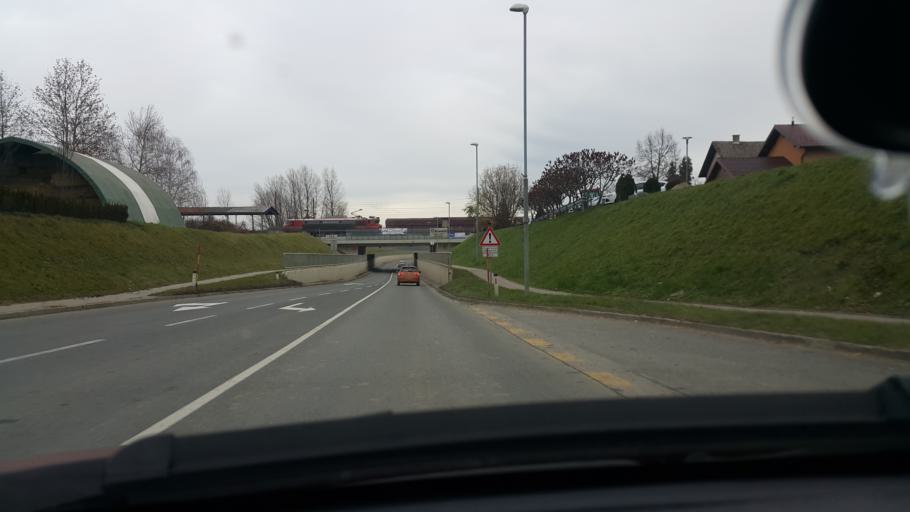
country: SI
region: Hoce-Slivnica
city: Spodnje Hoce
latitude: 46.5011
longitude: 15.6610
